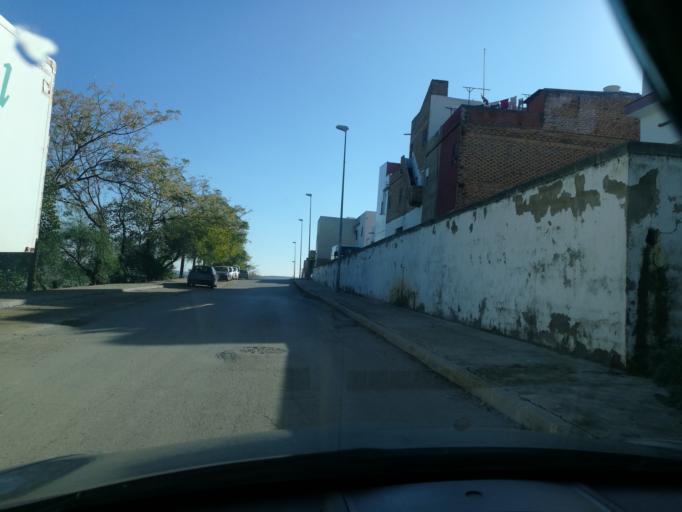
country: ES
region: Andalusia
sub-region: Provincia de Sevilla
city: La Campana
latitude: 37.5702
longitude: -5.4230
